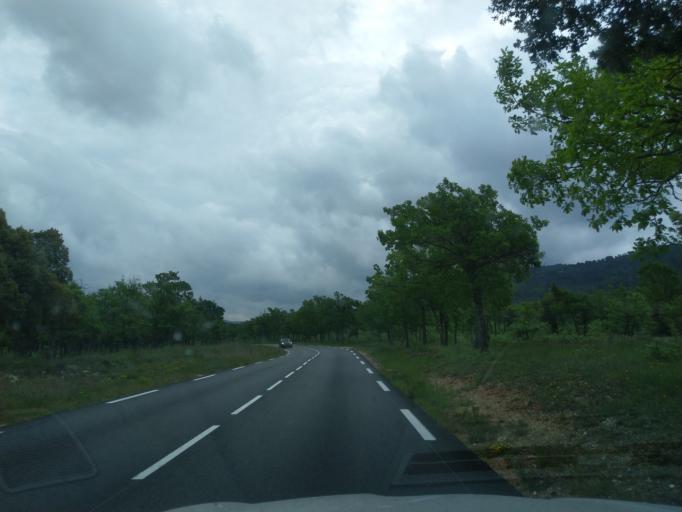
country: FR
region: Provence-Alpes-Cote d'Azur
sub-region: Departement du Var
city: Signes
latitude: 43.2770
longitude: 5.8104
